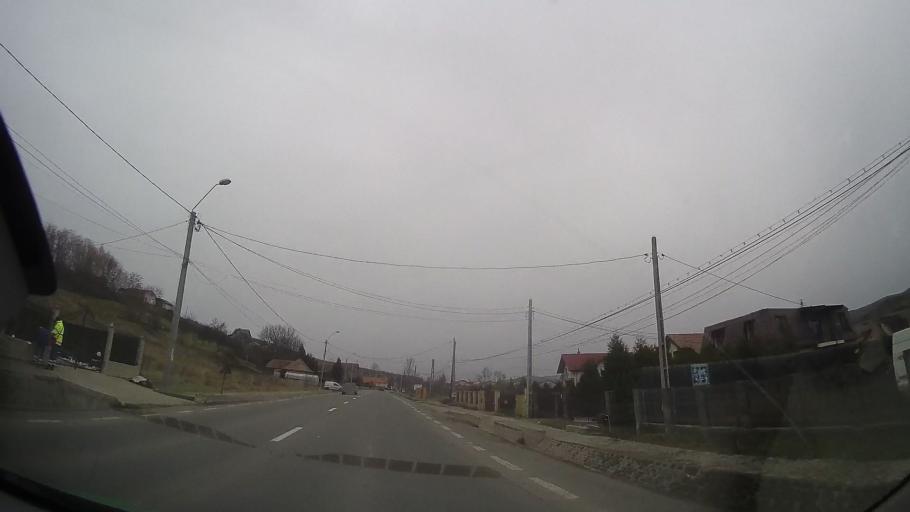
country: RO
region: Mures
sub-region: Comuna Ceausu de Campie
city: Ceausu de Campie
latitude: 46.6044
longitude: 24.5300
